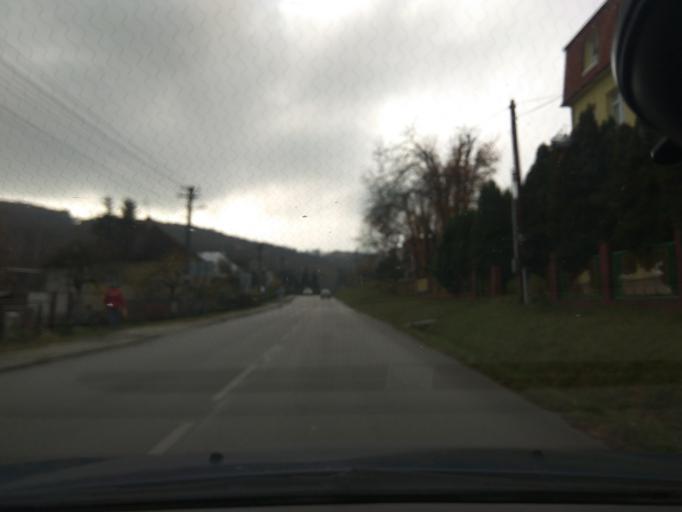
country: SK
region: Nitriansky
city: Stara Tura
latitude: 48.6949
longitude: 17.6874
